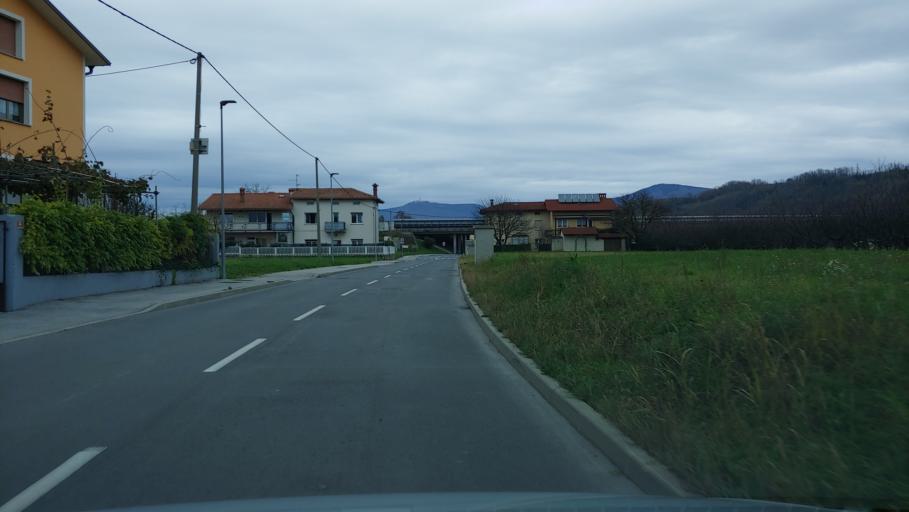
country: SI
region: Sempeter-Vrtojba
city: Vrtojba
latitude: 45.9189
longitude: 13.6390
